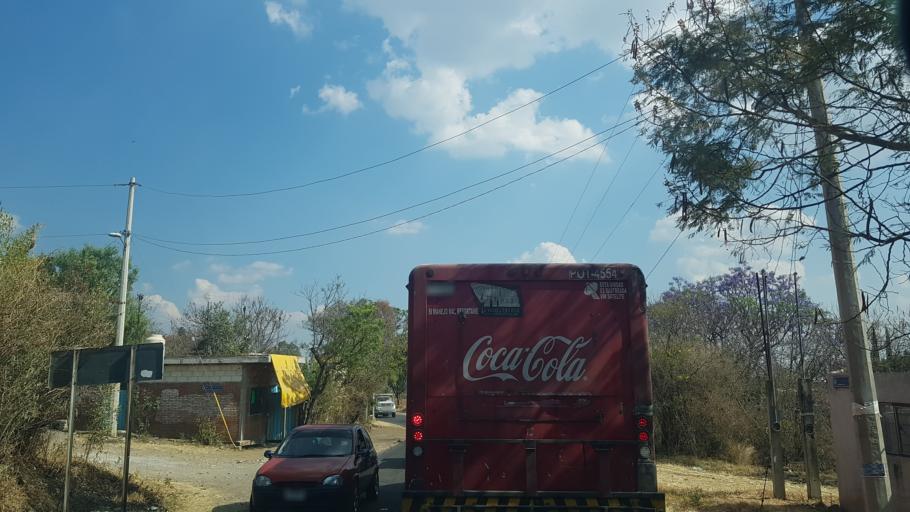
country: MX
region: Puebla
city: Atlixco
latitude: 18.9139
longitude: -98.4788
